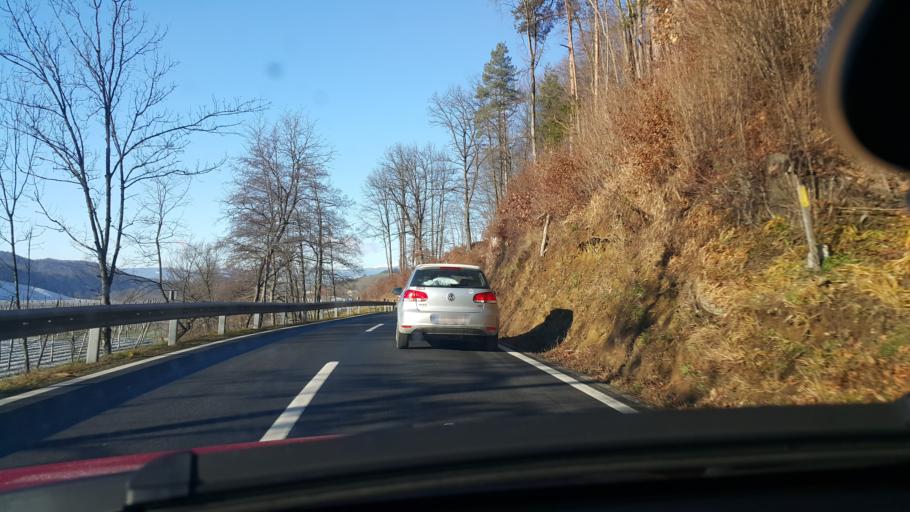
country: AT
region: Styria
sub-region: Politischer Bezirk Leibnitz
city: Leutschach
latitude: 46.6689
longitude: 15.4436
